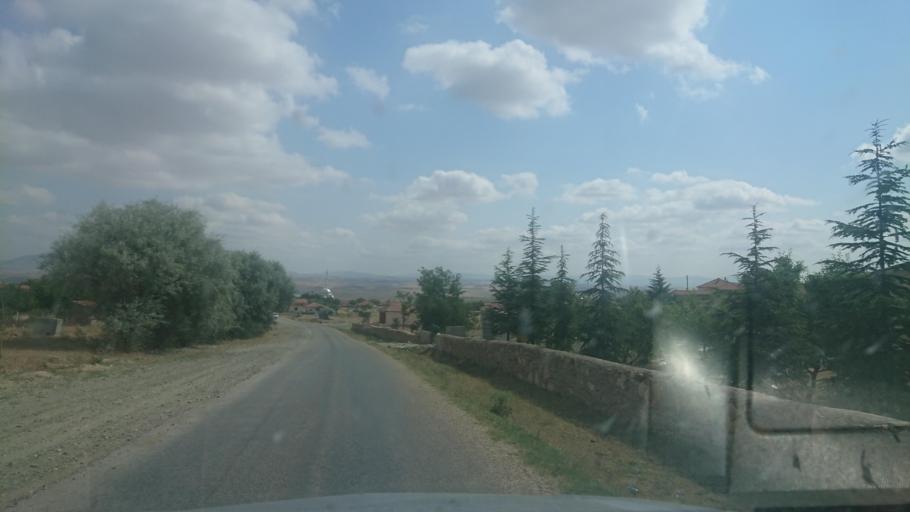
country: TR
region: Aksaray
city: Sariyahsi
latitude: 39.0103
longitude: 33.9436
